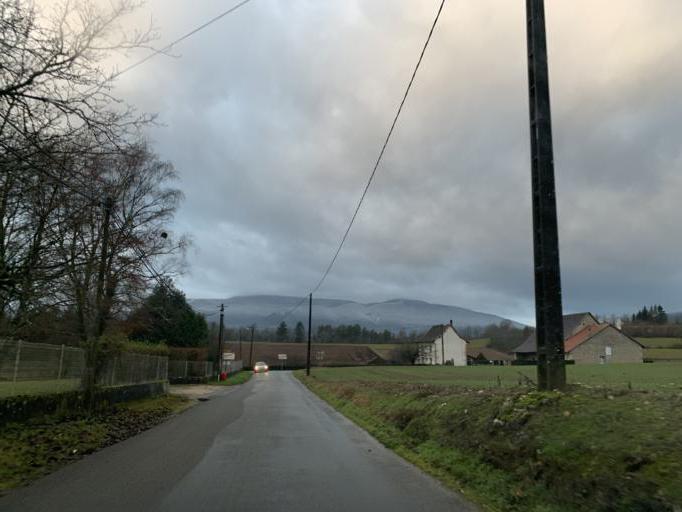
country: FR
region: Rhone-Alpes
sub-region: Departement de l'Ain
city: Belley
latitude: 45.8017
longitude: 5.6913
